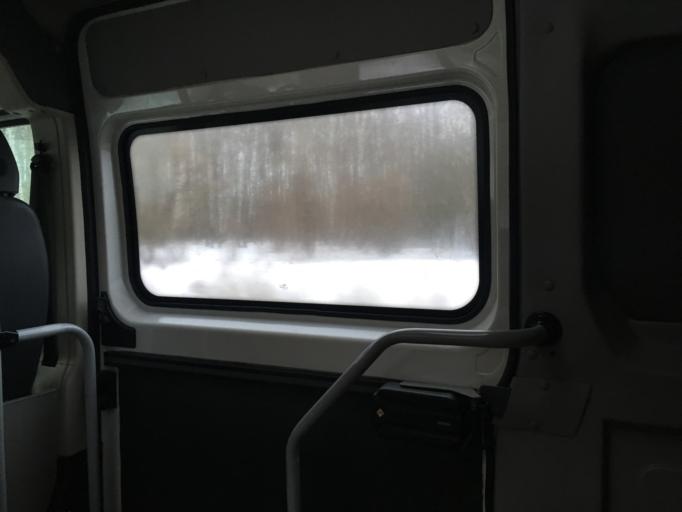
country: RU
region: Tula
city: Krapivna
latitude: 54.1227
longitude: 37.2409
